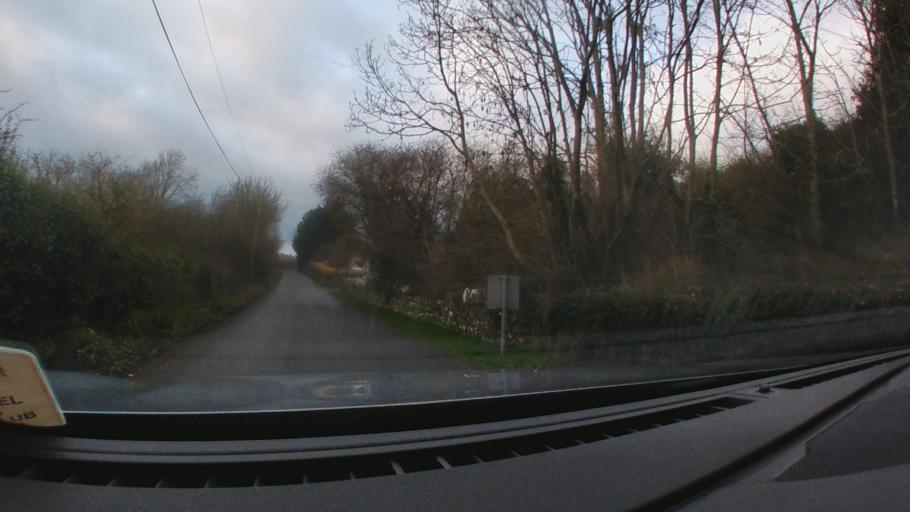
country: IE
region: Leinster
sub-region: Kilkenny
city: Thomastown
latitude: 52.5879
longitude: -7.1744
